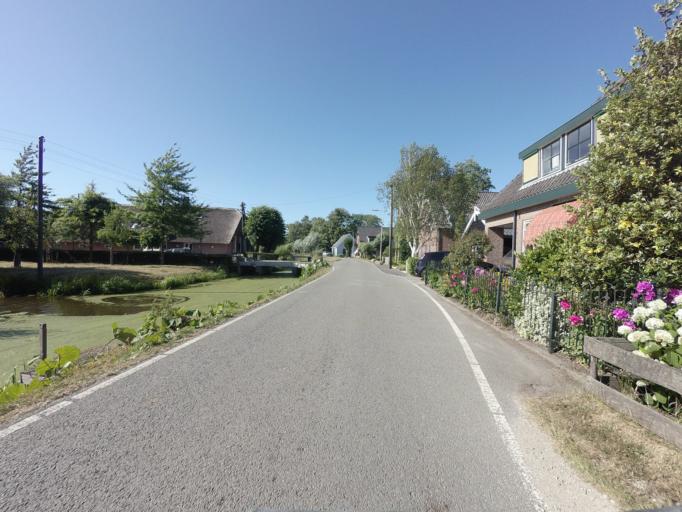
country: NL
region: South Holland
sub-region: Bodegraven-Reeuwijk
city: Bodegraven
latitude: 52.0778
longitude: 4.7349
